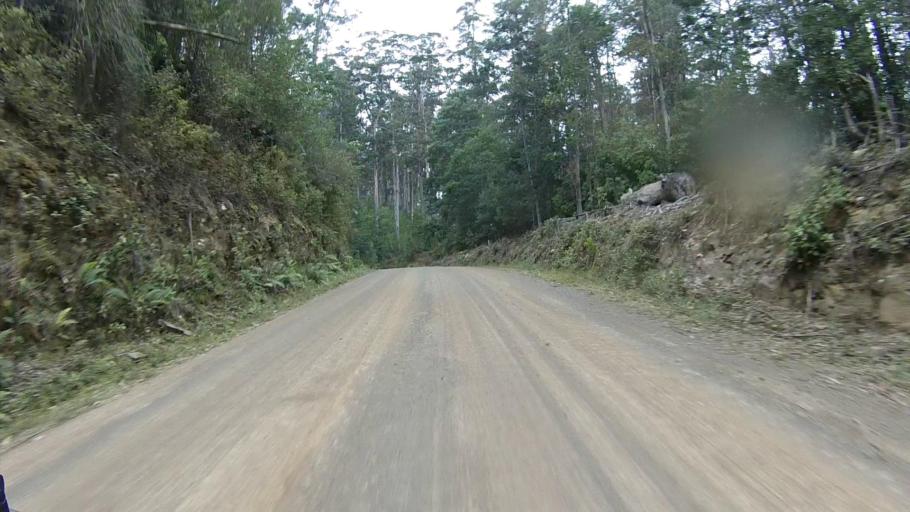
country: AU
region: Tasmania
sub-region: Sorell
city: Sorell
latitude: -42.7060
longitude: 147.8530
